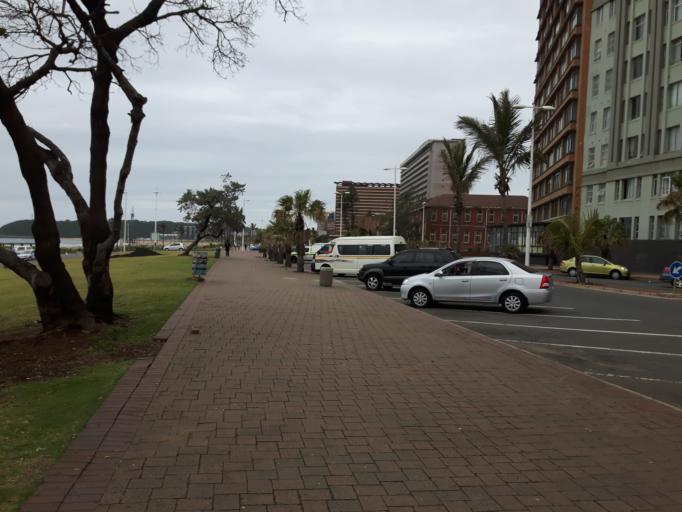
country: ZA
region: KwaZulu-Natal
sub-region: eThekwini Metropolitan Municipality
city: Durban
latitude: -29.8591
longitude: 31.0405
